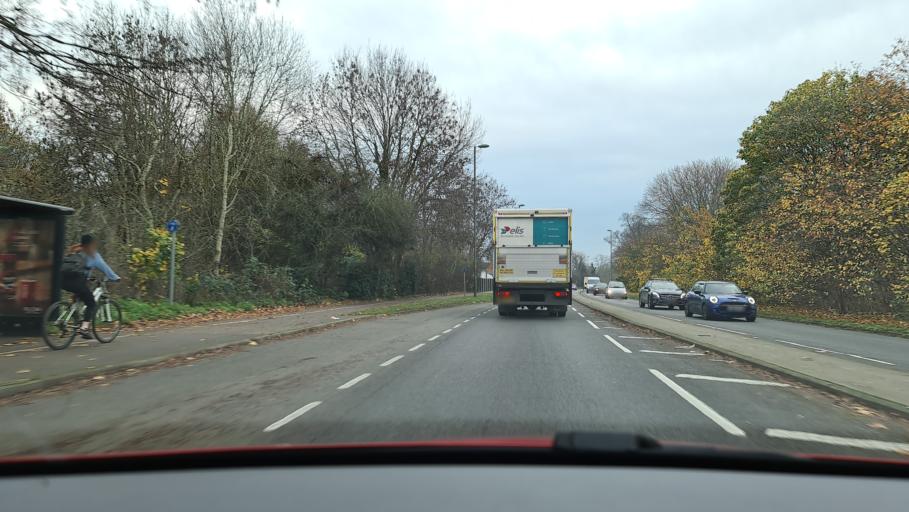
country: GB
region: England
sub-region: Surrey
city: East Molesey
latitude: 51.3976
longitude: -0.3425
